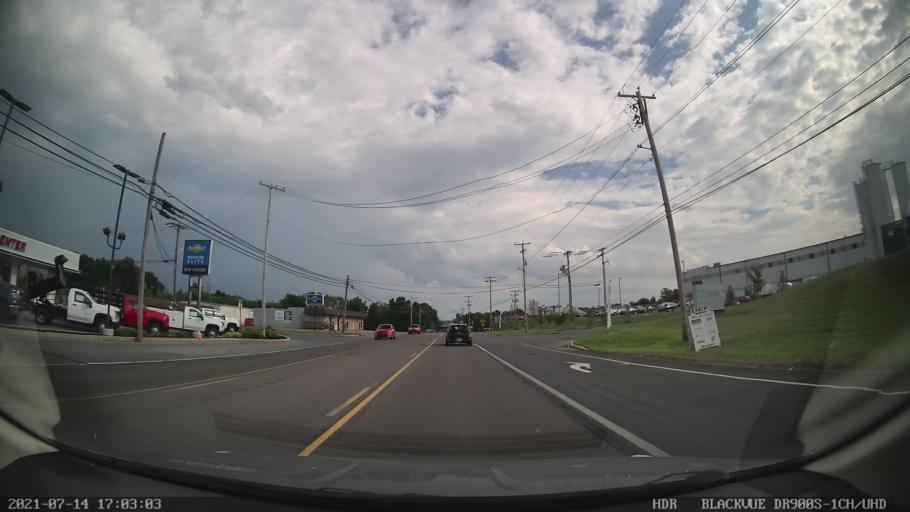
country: US
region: Pennsylvania
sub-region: Berks County
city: Muhlenberg Park
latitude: 40.3968
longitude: -75.9357
